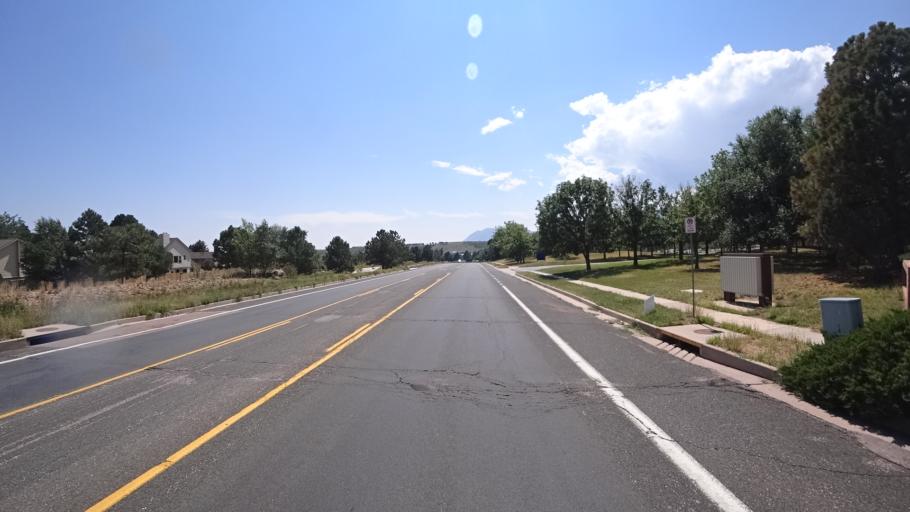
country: US
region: Colorado
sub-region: El Paso County
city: Manitou Springs
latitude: 38.9042
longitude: -104.8715
